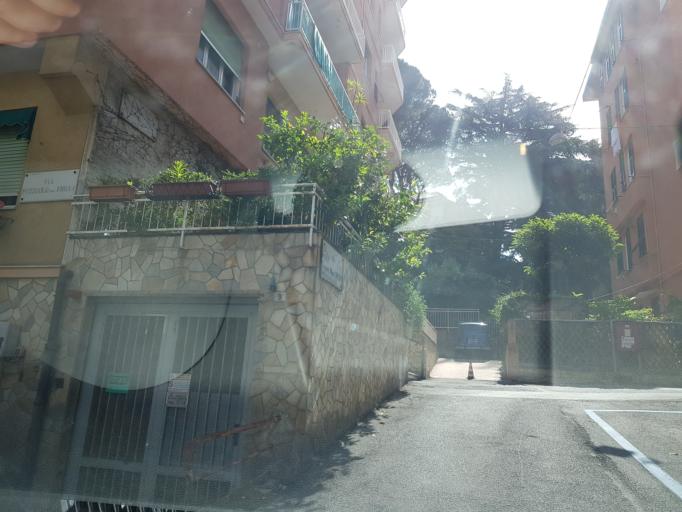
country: IT
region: Liguria
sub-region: Provincia di Genova
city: Genoa
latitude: 44.4008
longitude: 8.9657
